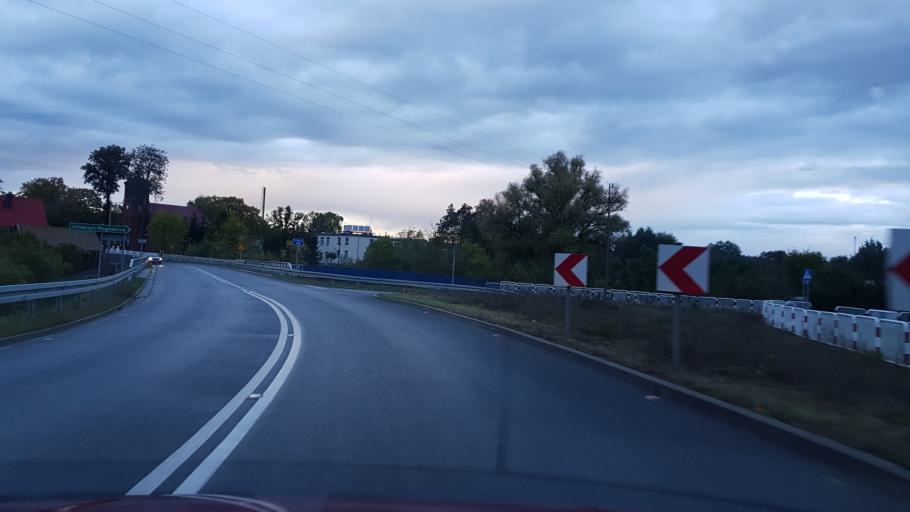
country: PL
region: Greater Poland Voivodeship
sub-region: Powiat pilski
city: Smilowo
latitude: 53.2227
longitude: 16.8724
